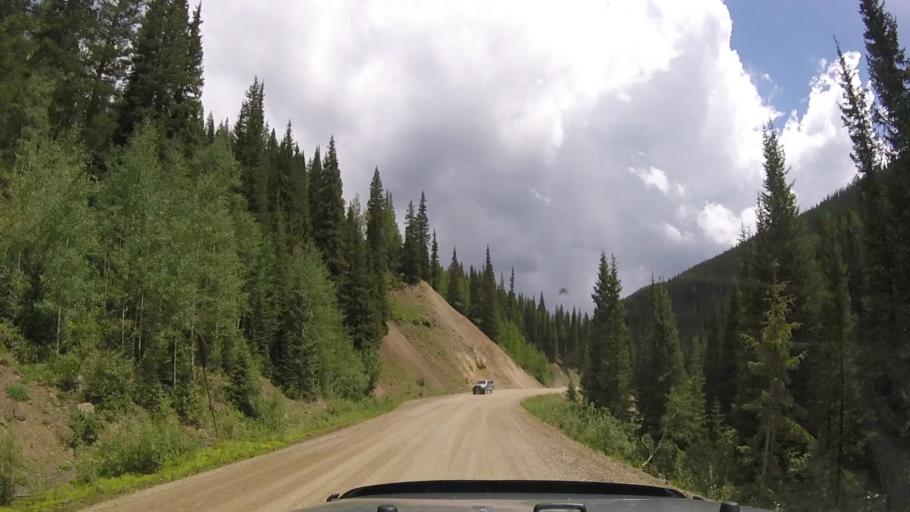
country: US
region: Colorado
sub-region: San Juan County
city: Silverton
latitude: 37.8380
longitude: -107.6784
